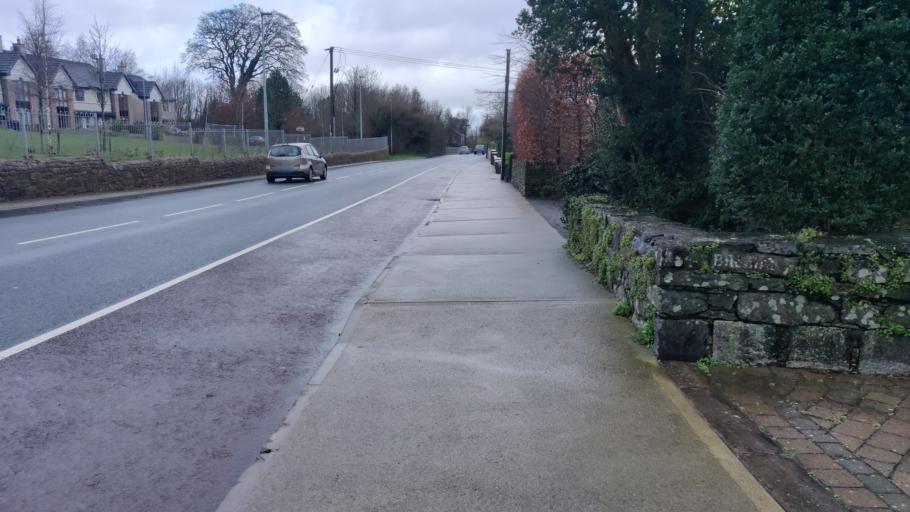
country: IE
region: Munster
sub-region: County Cork
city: Carrigaline
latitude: 51.8652
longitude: -8.4142
